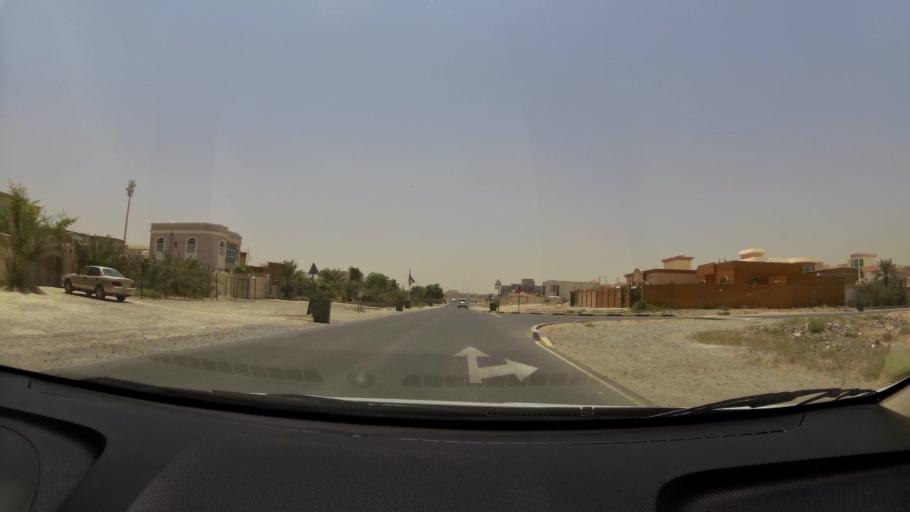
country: AE
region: Ajman
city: Ajman
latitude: 25.4101
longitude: 55.5232
